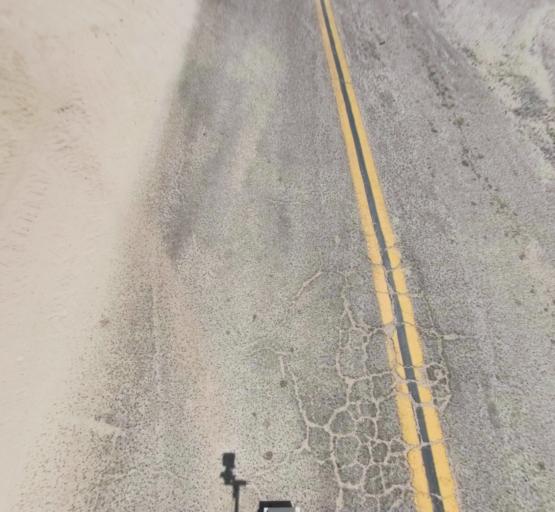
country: US
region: California
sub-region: Fresno County
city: Kerman
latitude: 36.8223
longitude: -120.1509
